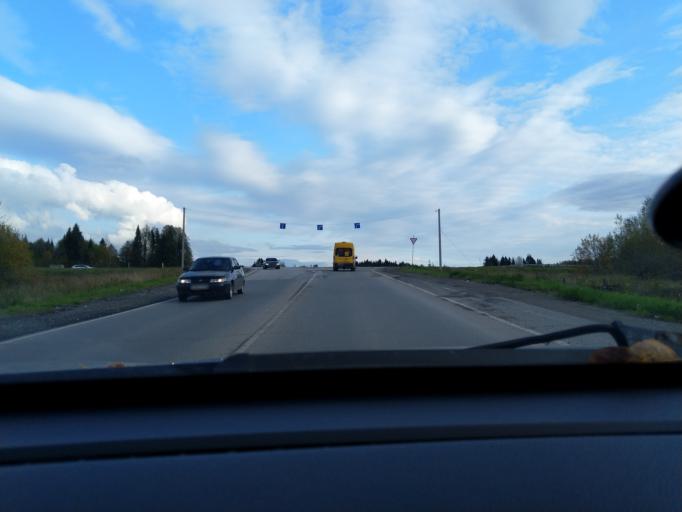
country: RU
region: Perm
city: Polazna
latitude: 58.2748
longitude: 56.4158
